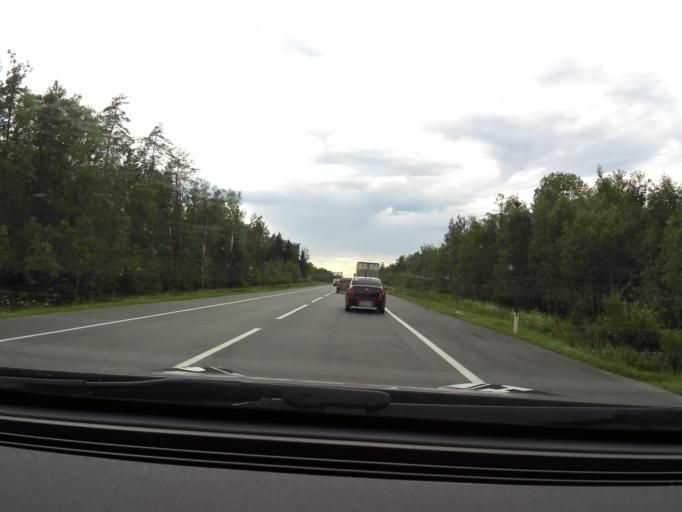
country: RU
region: Vladimir
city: Raduzhnyy
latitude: 56.0691
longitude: 40.2964
